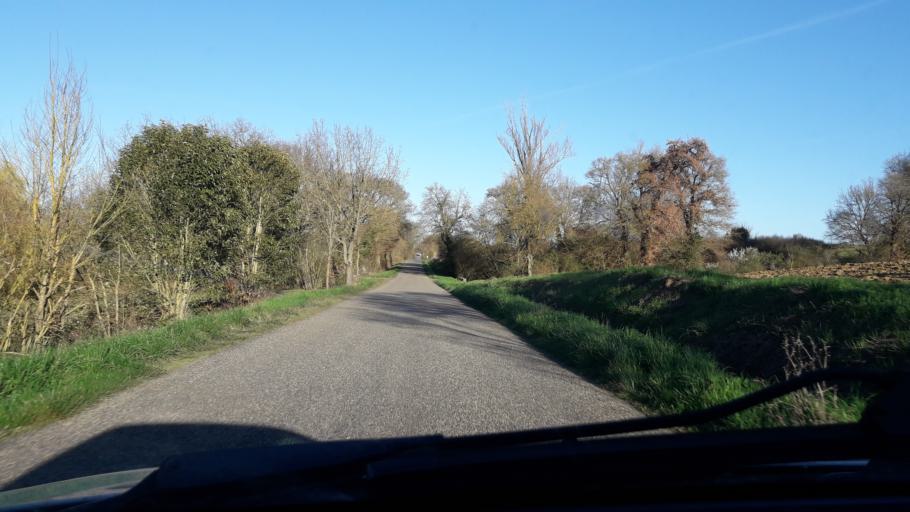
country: FR
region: Midi-Pyrenees
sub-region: Departement du Gers
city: Gimont
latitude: 43.6256
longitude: 0.9903
